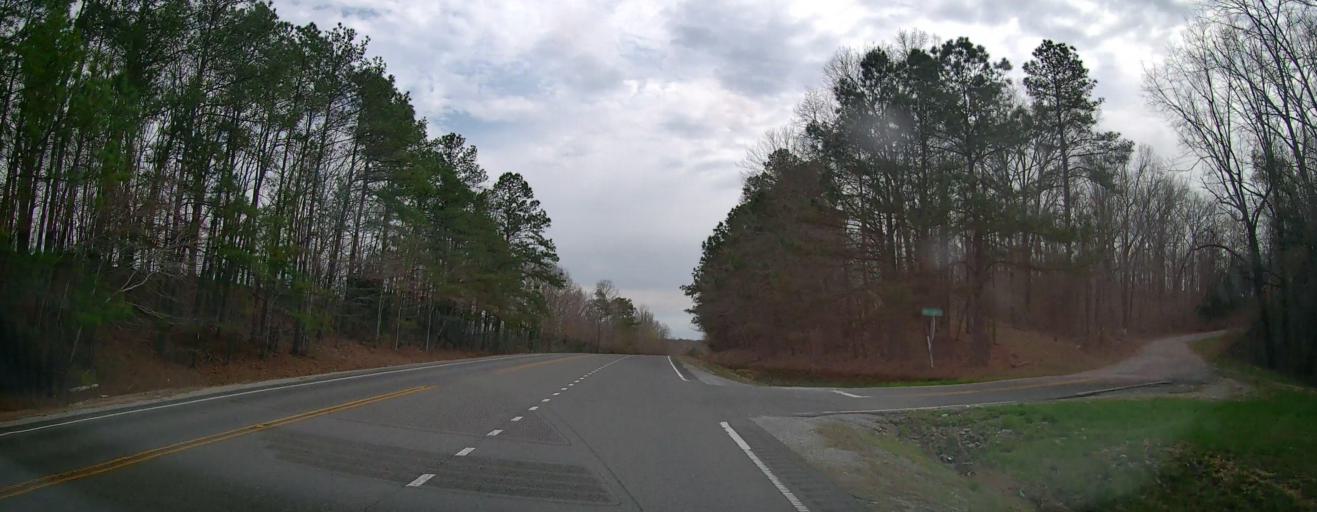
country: US
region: Alabama
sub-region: Marion County
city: Hamilton
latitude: 34.0554
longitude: -87.9664
